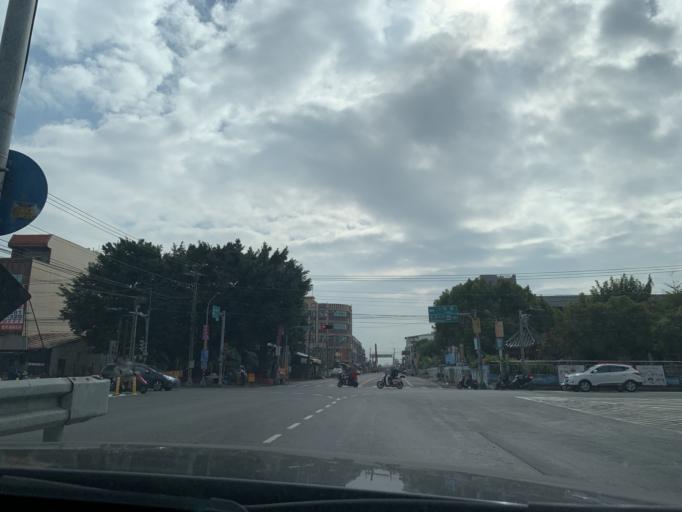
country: TW
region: Taiwan
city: Fengshan
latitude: 22.4631
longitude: 120.4621
